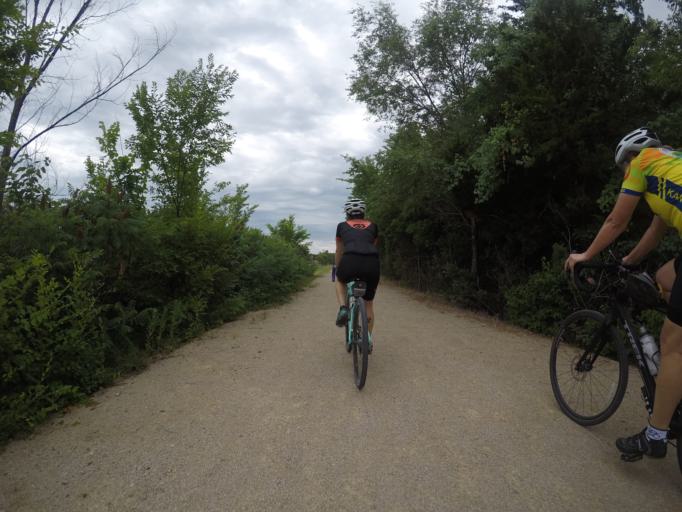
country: US
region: Kansas
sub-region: Anderson County
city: Garnett
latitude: 38.2913
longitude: -95.2421
